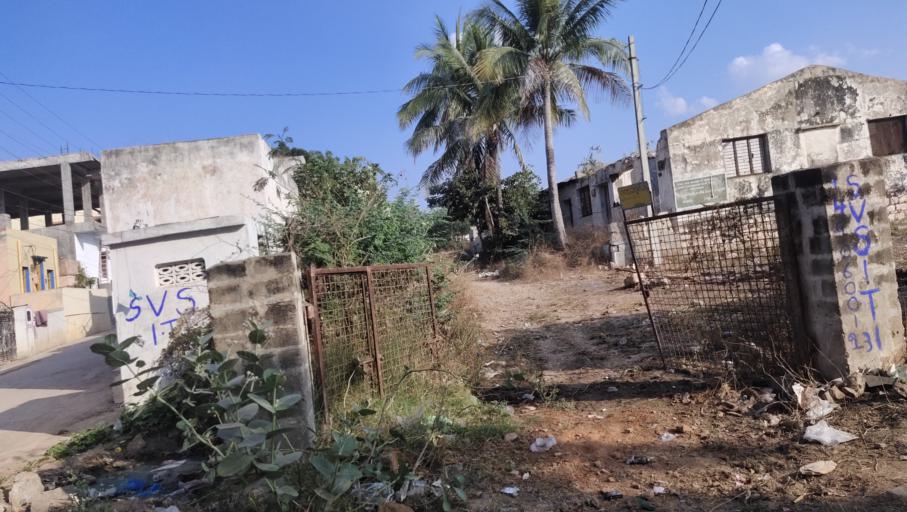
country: IN
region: Andhra Pradesh
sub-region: Anantapur
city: Tadpatri
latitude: 14.9334
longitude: 77.8633
